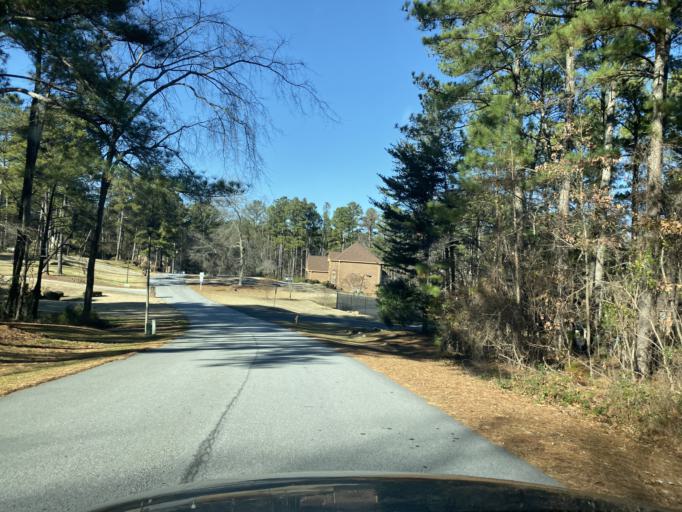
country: US
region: Georgia
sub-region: DeKalb County
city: Pine Mountain
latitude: 33.6799
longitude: -84.1654
